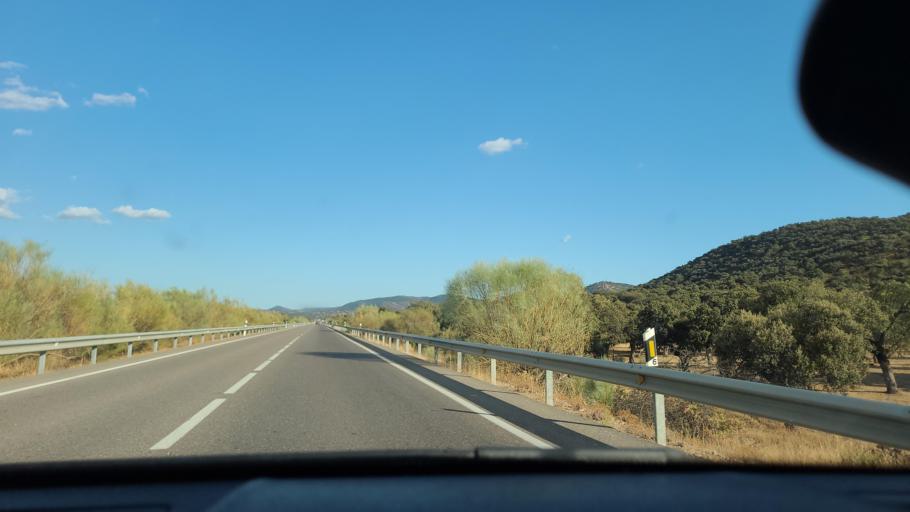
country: ES
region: Andalusia
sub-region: Province of Cordoba
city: Belmez
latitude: 38.2244
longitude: -5.1582
